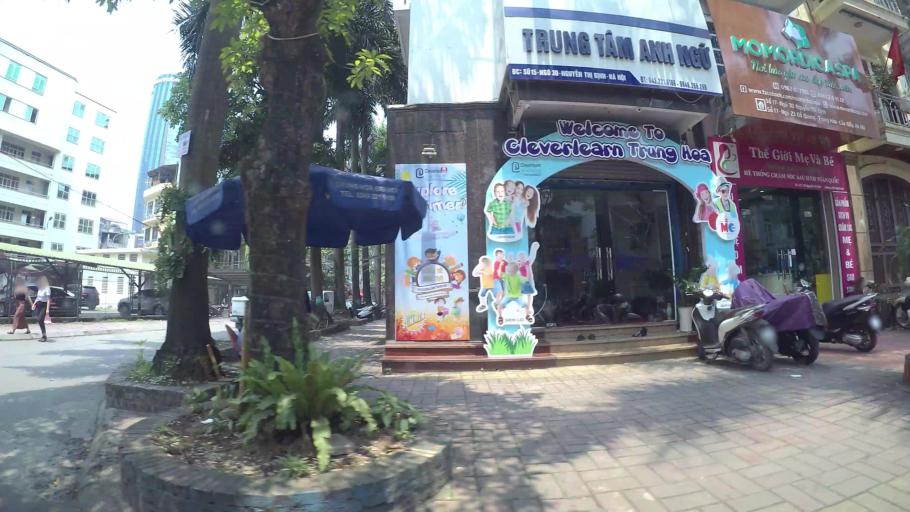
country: VN
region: Ha Noi
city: Thanh Xuan
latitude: 21.0115
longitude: 105.8030
